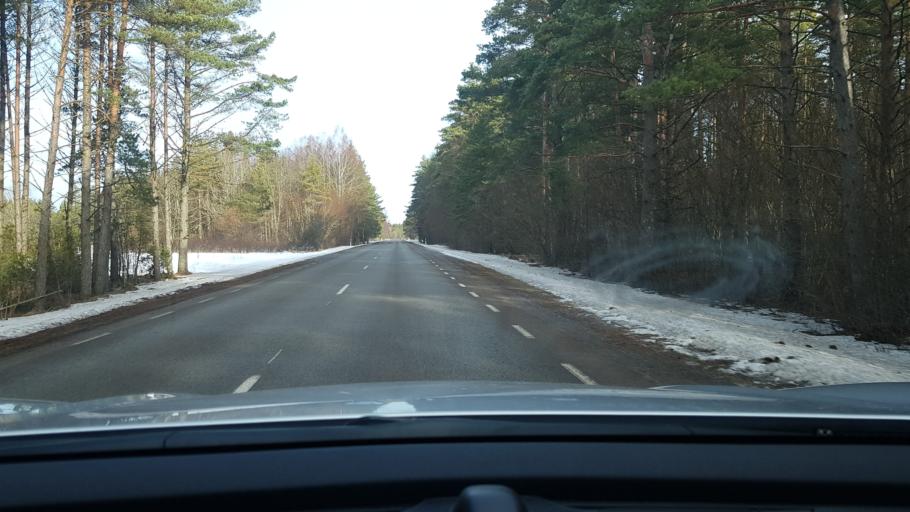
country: EE
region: Saare
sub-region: Kuressaare linn
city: Kuressaare
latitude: 58.4729
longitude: 22.7029
